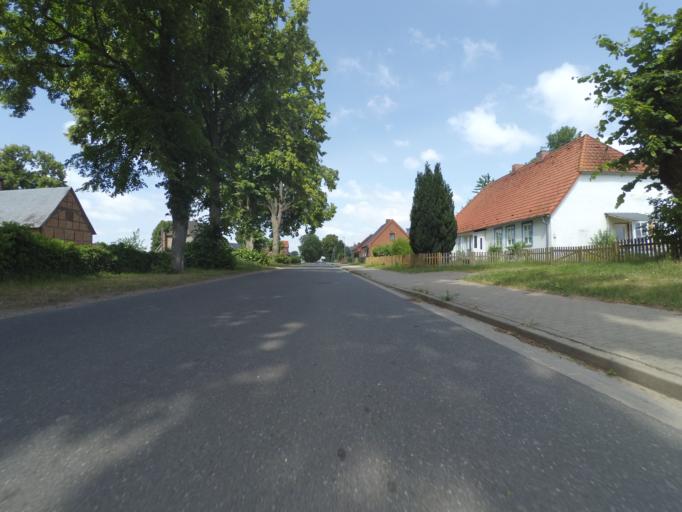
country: DE
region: Mecklenburg-Vorpommern
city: Lubz
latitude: 53.4369
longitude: 12.0116
